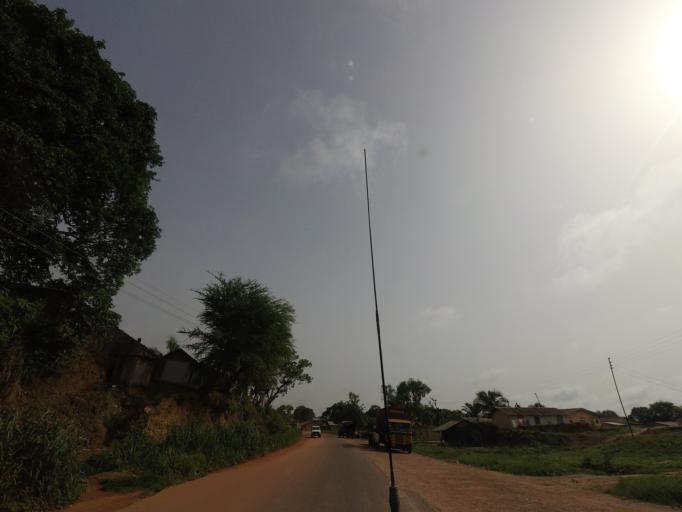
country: SL
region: Southern Province
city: Bo
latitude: 7.9397
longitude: -11.7260
